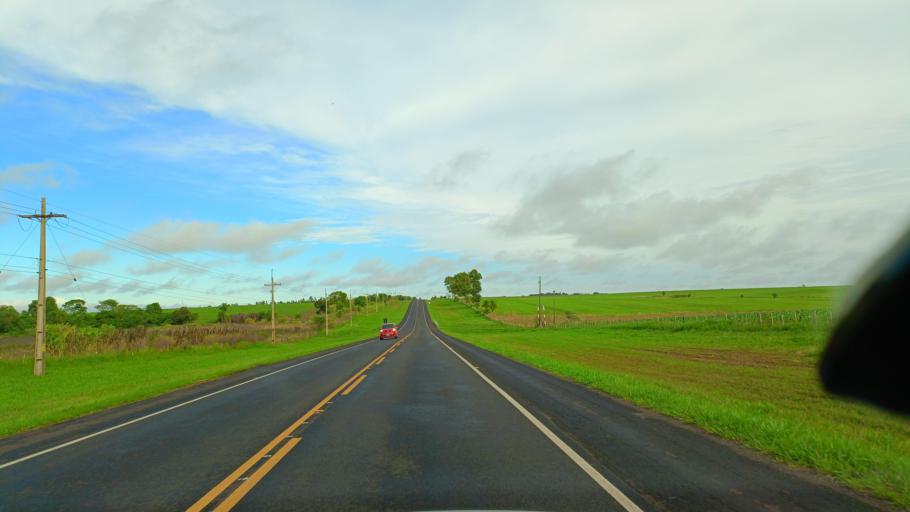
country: PY
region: Misiones
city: San Patricio
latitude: -26.9971
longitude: -56.7713
